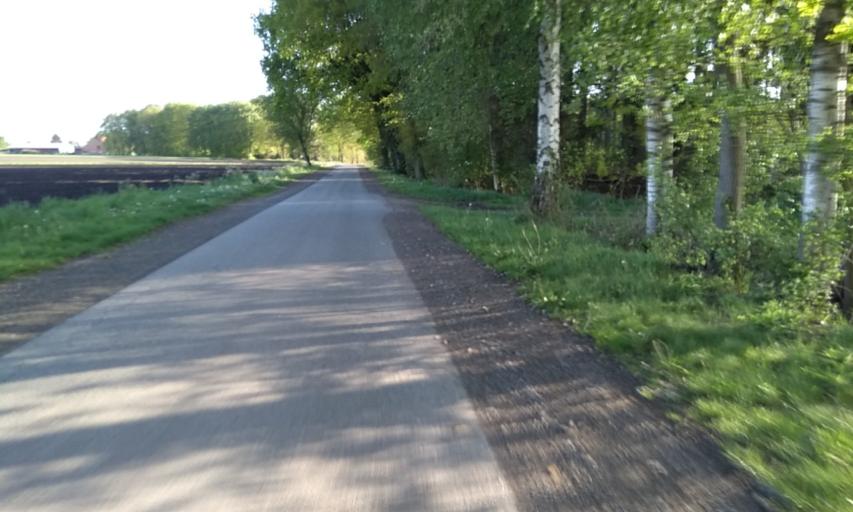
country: DE
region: Lower Saxony
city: Harsefeld
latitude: 53.4216
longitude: 9.5523
